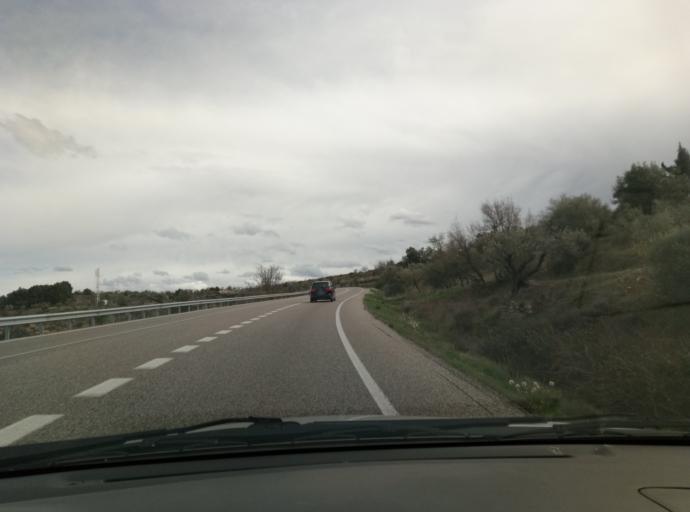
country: ES
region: Catalonia
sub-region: Provincia de Lleida
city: Ciutadilla
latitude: 41.5589
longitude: 1.1343
